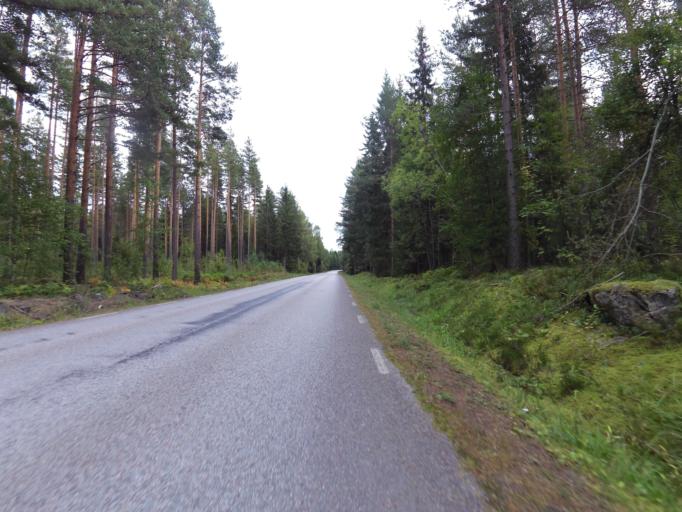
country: SE
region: Gaevleborg
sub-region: Gavle Kommun
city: Valbo
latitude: 60.6621
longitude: 16.9653
